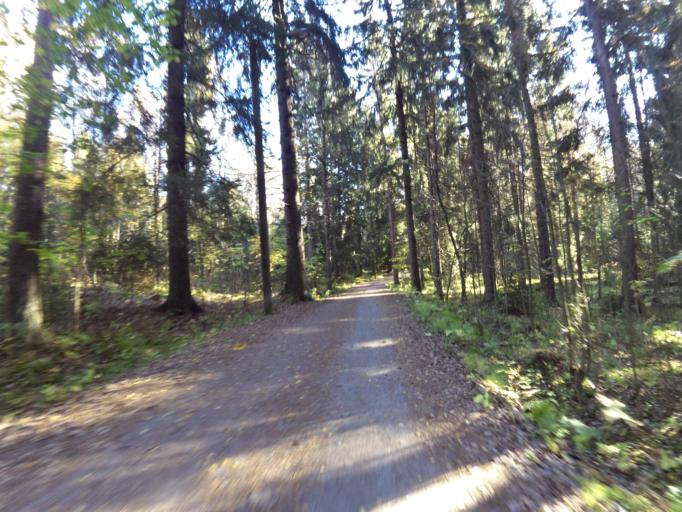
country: FI
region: Uusimaa
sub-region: Helsinki
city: Kauniainen
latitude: 60.1785
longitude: 24.7099
